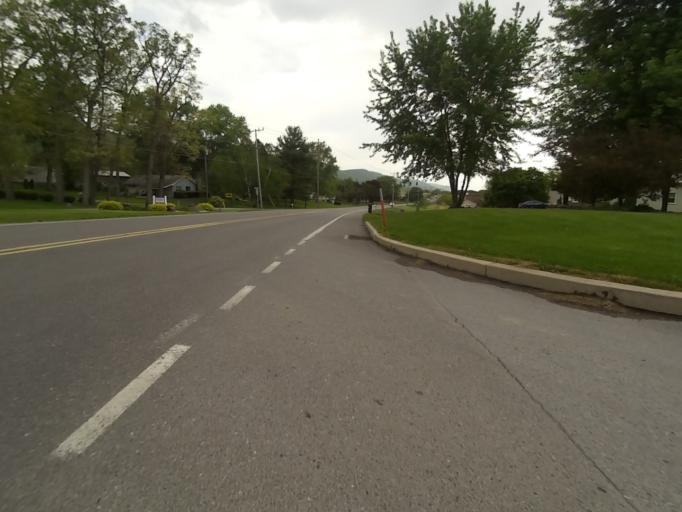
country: US
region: Pennsylvania
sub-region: Centre County
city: Zion
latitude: 40.9090
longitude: -77.6822
